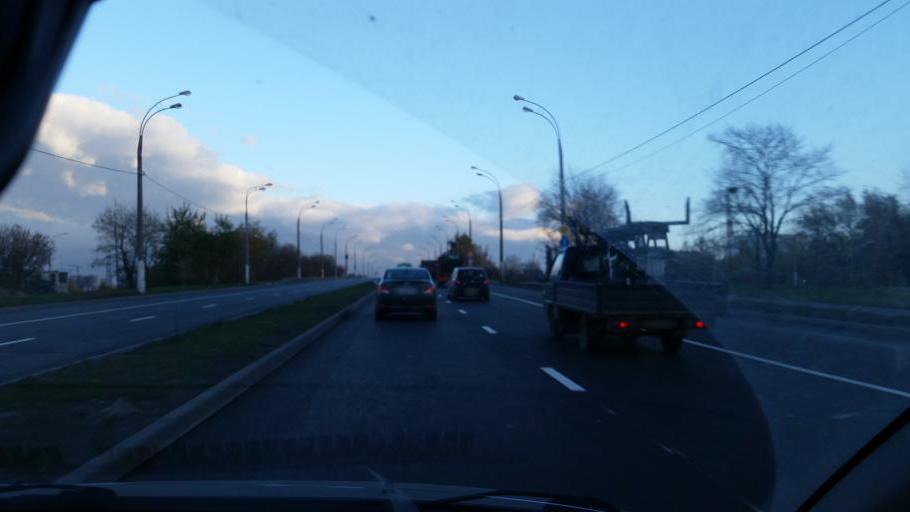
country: RU
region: Moskovskaya
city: Biryulevo Zapadnoye
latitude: 55.6058
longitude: 37.6284
